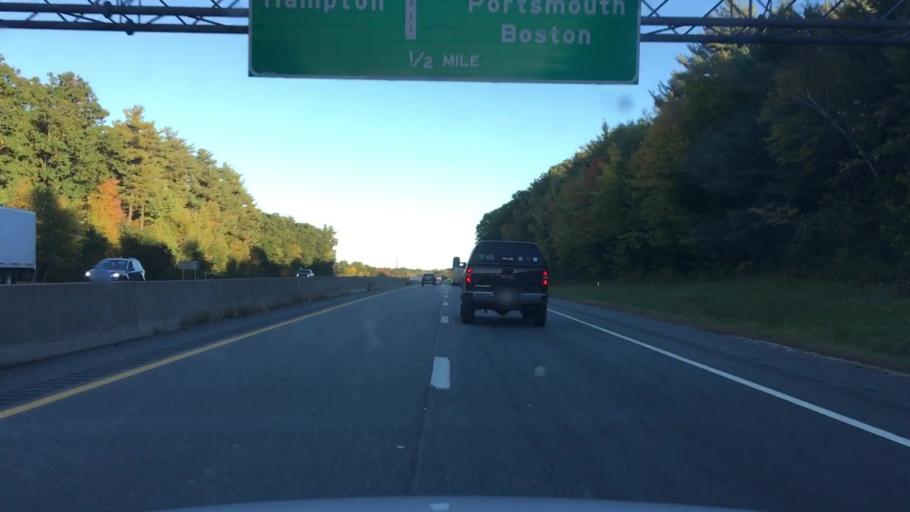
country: US
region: New Hampshire
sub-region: Rockingham County
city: Hampton
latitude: 42.9633
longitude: -70.8716
